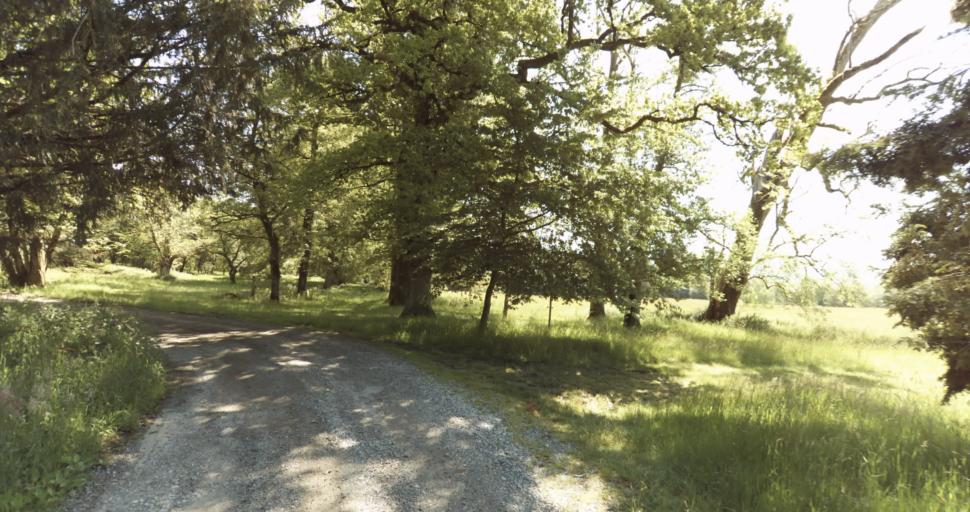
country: FR
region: Limousin
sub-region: Departement de la Haute-Vienne
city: Le Vigen
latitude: 45.7241
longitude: 1.3025
